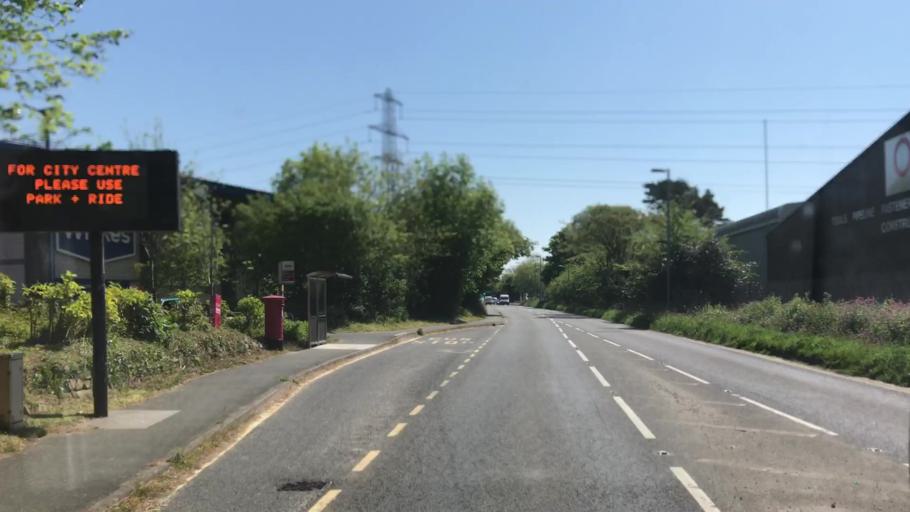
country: GB
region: England
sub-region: Cornwall
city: Chacewater
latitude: 50.2639
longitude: -5.1237
